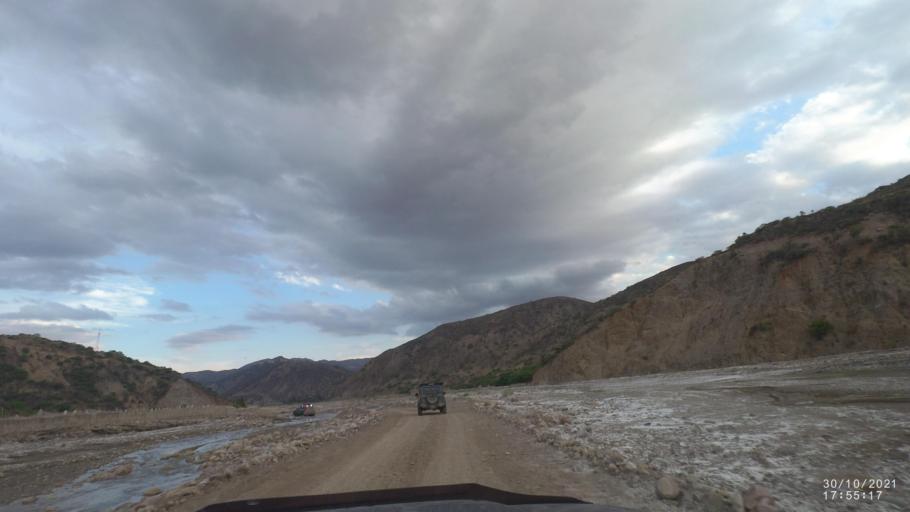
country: BO
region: Cochabamba
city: Sipe Sipe
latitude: -17.5453
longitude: -66.4861
